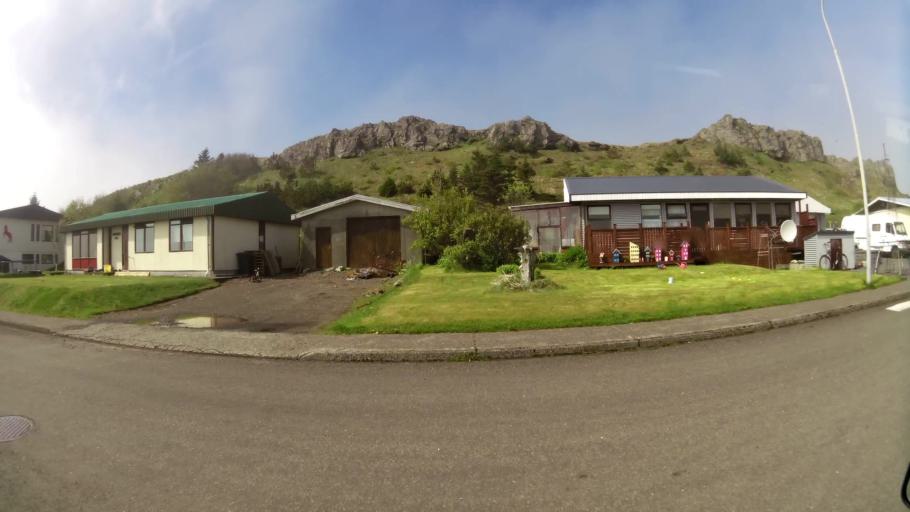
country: IS
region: East
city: Reydarfjoerdur
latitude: 64.6540
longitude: -14.2820
